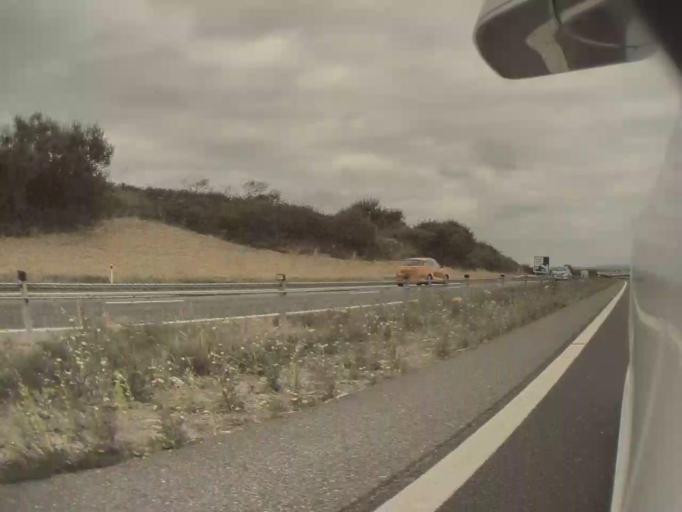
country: GB
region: Wales
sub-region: Anglesey
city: Llanfachraeth
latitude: 53.2800
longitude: -4.5318
